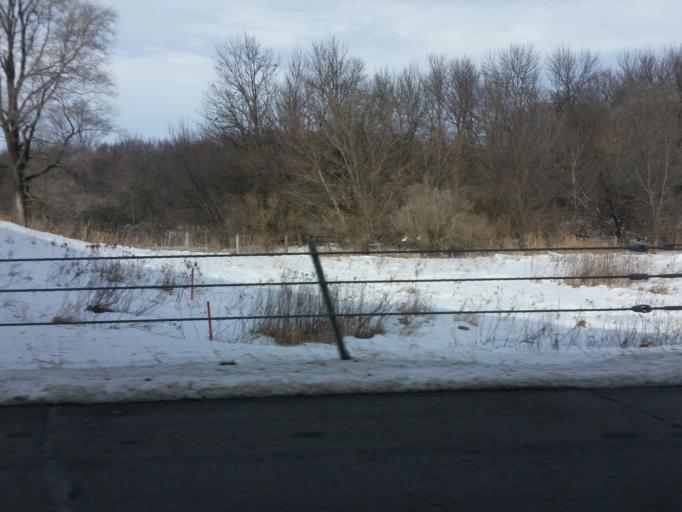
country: US
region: Iowa
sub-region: Buchanan County
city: Independence
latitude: 42.4608
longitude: -91.7113
